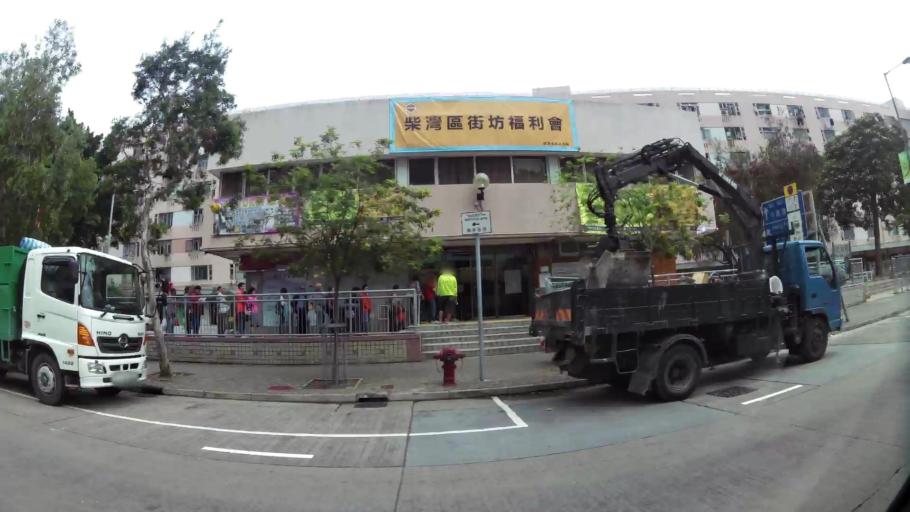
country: HK
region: Wanchai
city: Wan Chai
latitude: 22.2651
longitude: 114.2414
